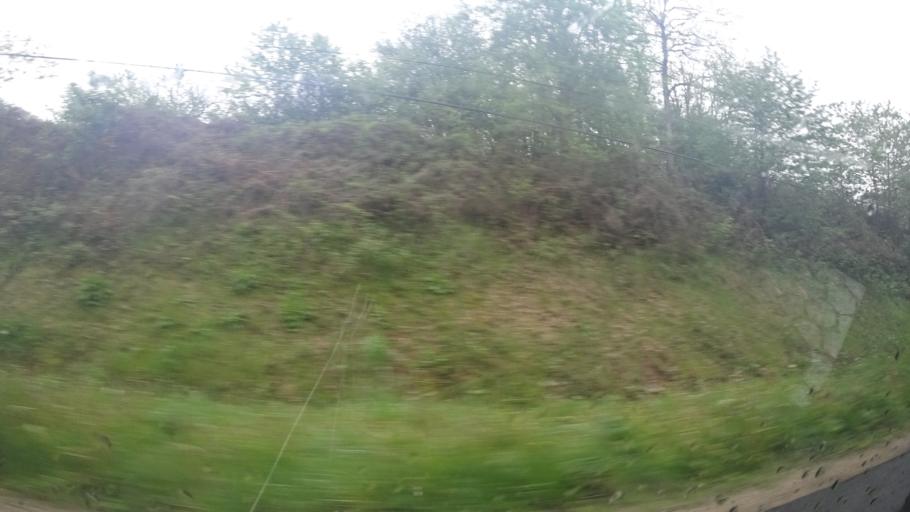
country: FR
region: Midi-Pyrenees
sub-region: Departement de l'Aveyron
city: Laissac
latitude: 44.2827
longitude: 2.8530
